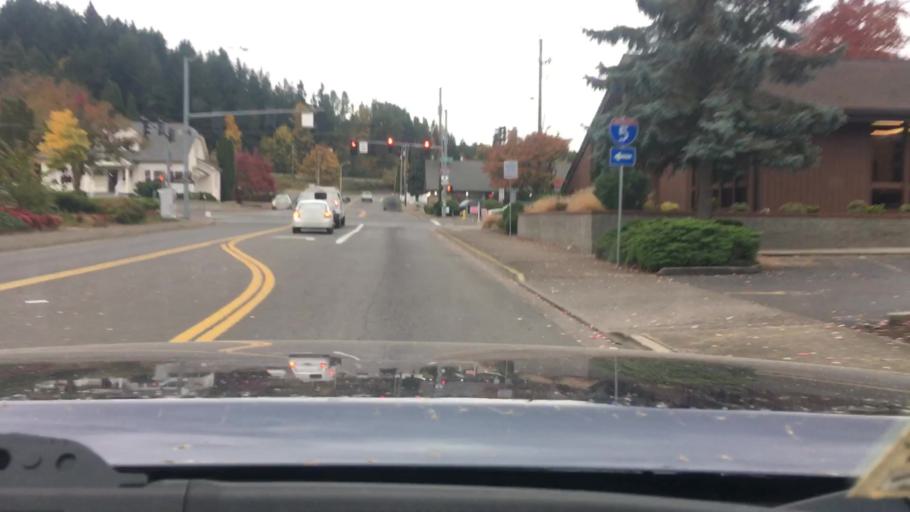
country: US
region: Oregon
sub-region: Lane County
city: Cottage Grove
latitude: 43.7978
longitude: -123.0488
